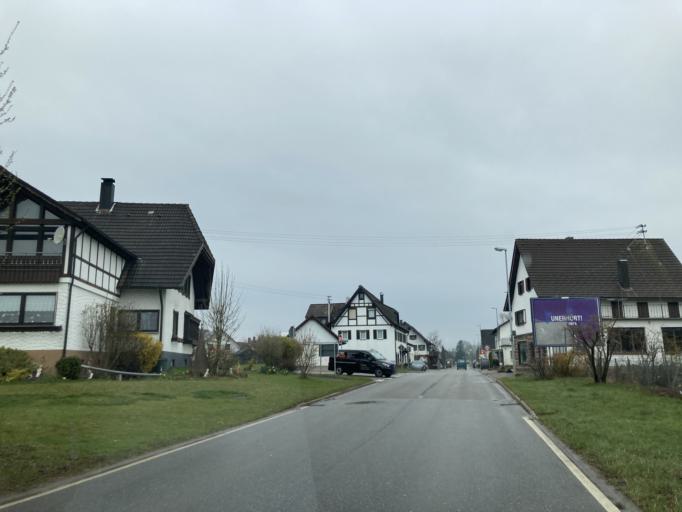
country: DE
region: Baden-Wuerttemberg
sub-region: Freiburg Region
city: Dornhan
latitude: 48.3232
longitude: 8.4679
